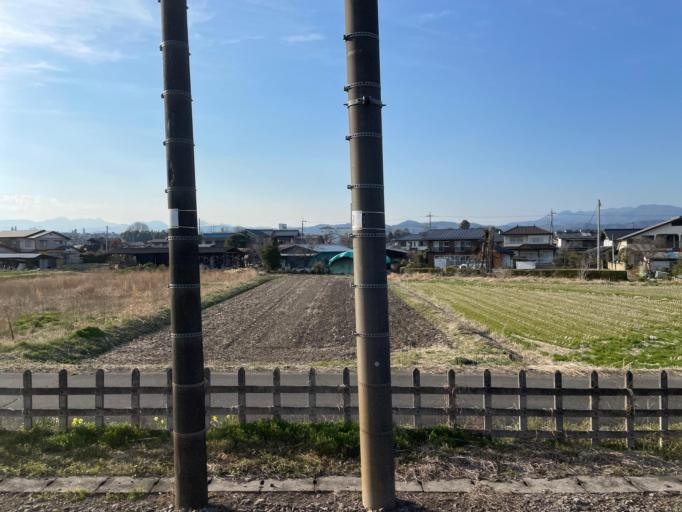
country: JP
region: Gunma
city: Annaka
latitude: 36.3140
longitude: 138.8849
